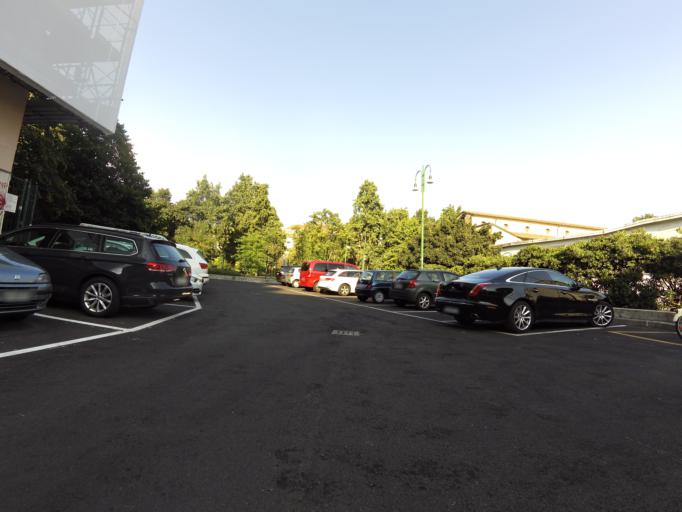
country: IT
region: Lombardy
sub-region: Citta metropolitana di Milano
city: Milano
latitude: 45.4552
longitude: 9.1808
